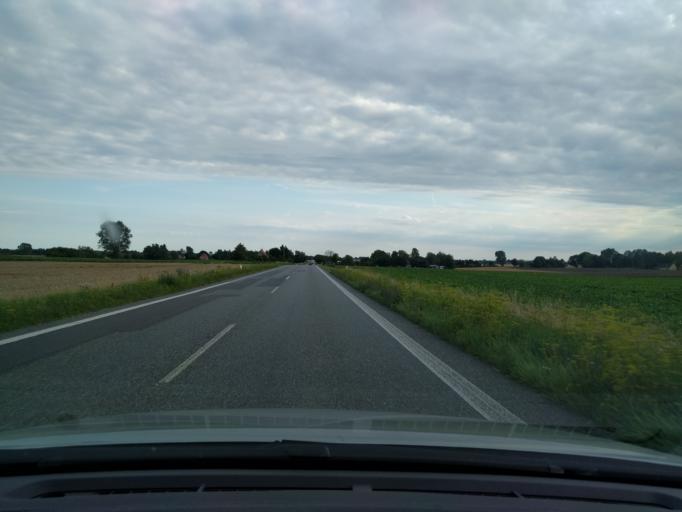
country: DK
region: Zealand
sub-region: Guldborgsund Kommune
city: Stubbekobing
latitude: 54.8244
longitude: 11.9947
